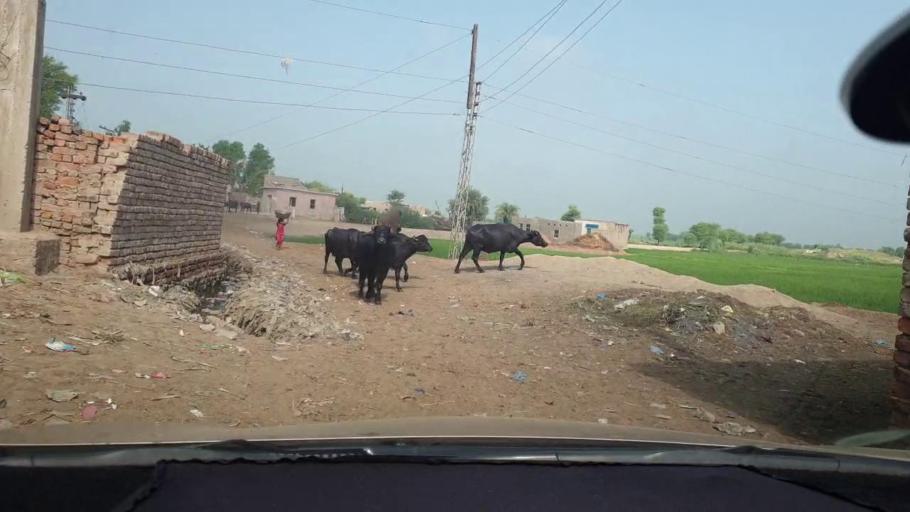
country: PK
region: Sindh
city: Kambar
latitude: 27.5434
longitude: 68.0460
